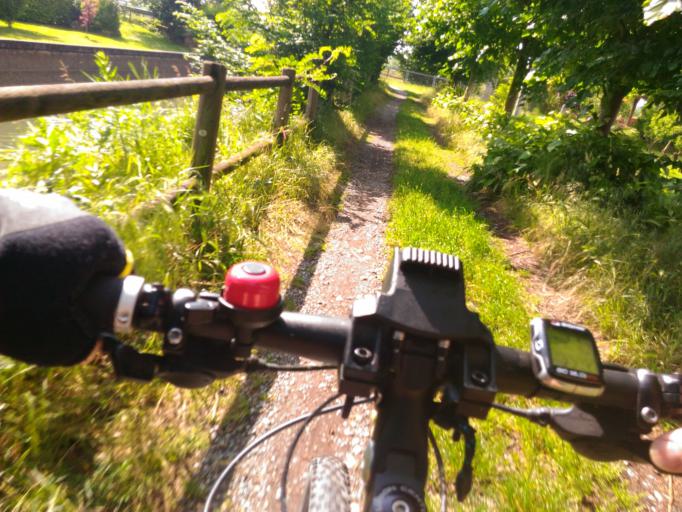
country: IT
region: Lombardy
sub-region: Provincia di Lodi
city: Massalengo-Motta Vigana
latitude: 45.2720
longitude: 9.5025
